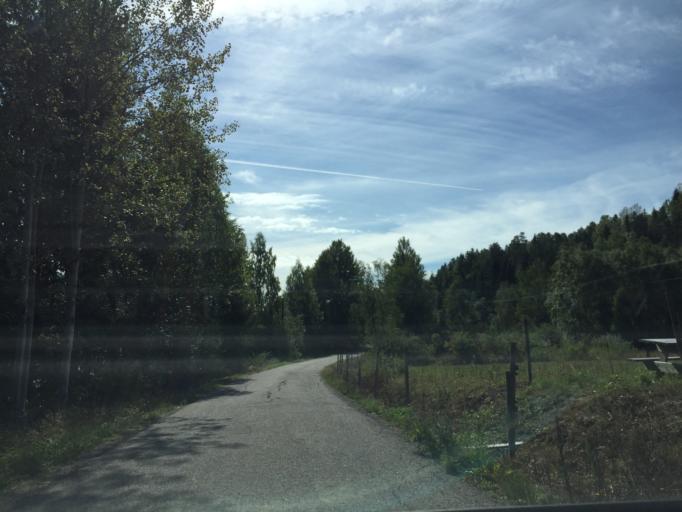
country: NO
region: Vestfold
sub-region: Hof
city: Hof
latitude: 59.4714
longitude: 10.1438
